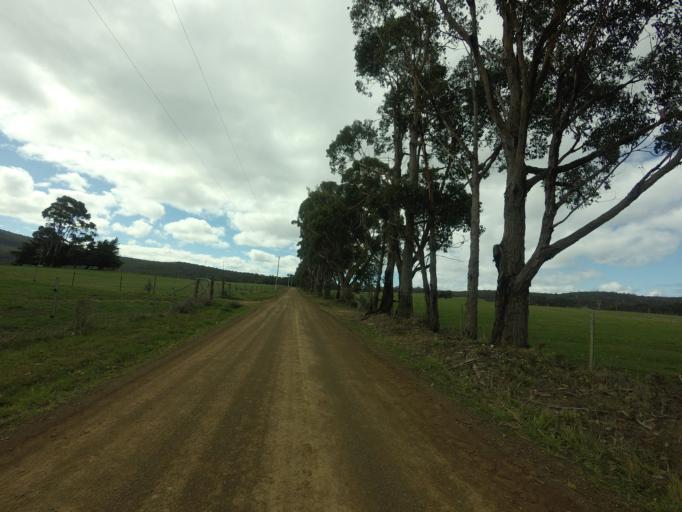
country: AU
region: Tasmania
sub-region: Huon Valley
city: Geeveston
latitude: -43.4329
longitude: 146.9885
